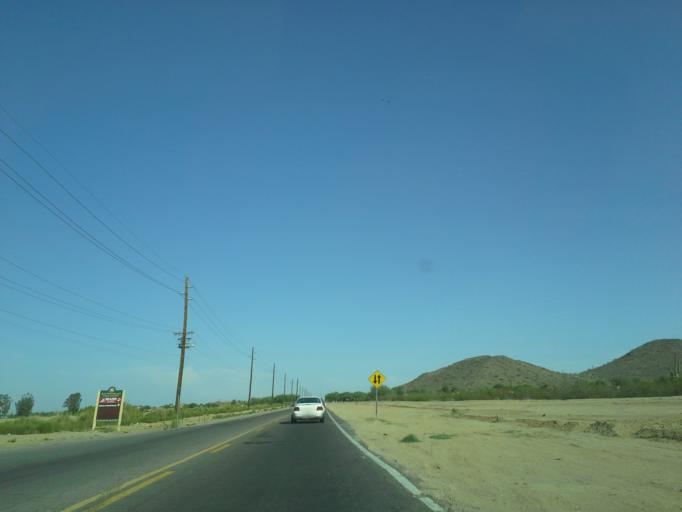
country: US
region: Arizona
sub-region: Pinal County
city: San Tan Valley
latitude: 33.1763
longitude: -111.5801
